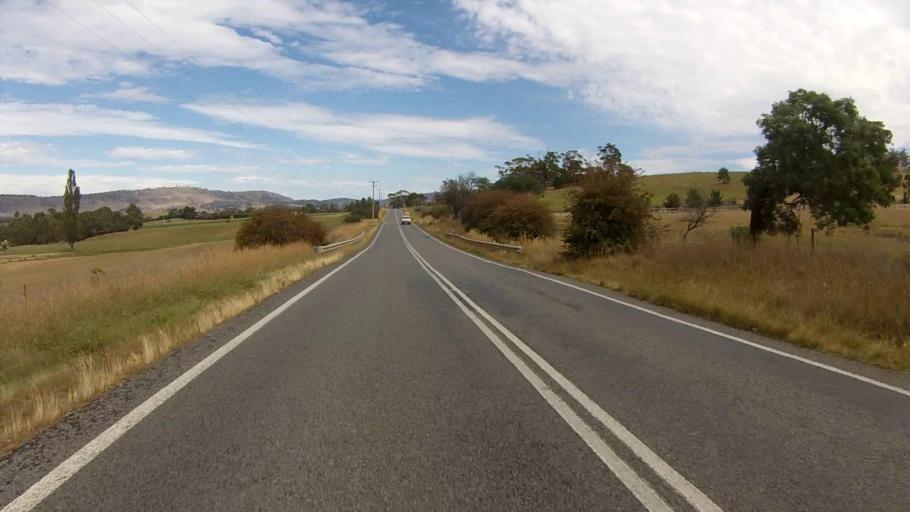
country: AU
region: Tasmania
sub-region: Sorell
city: Sorell
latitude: -42.6932
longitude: 147.4750
